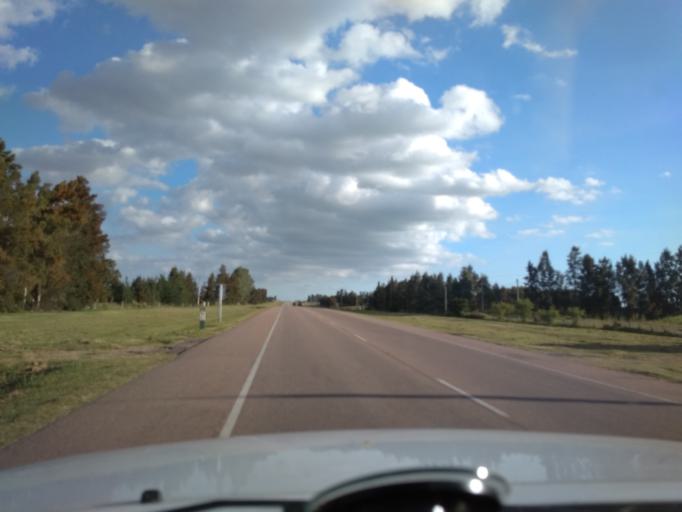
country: UY
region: Canelones
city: Canelones
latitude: -34.4024
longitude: -56.2576
